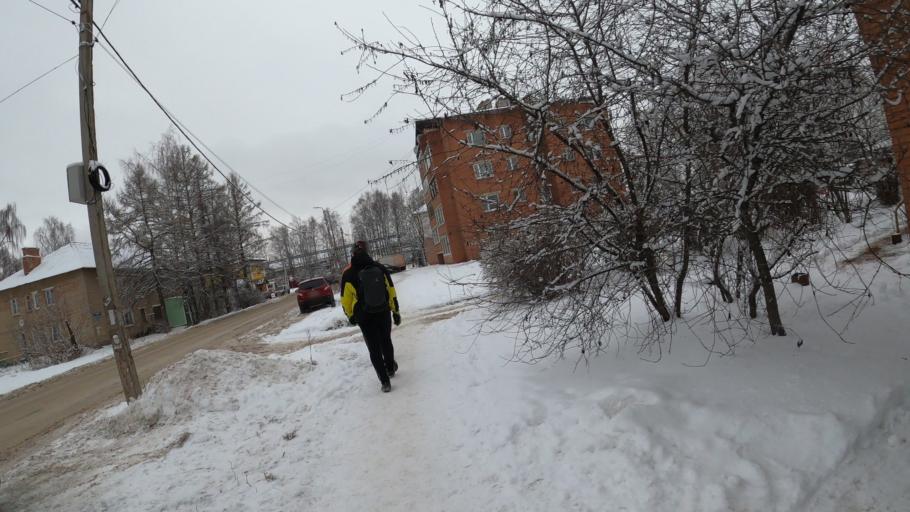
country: RU
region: Jaroslavl
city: Pereslavl'-Zalesskiy
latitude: 56.7401
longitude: 38.8866
